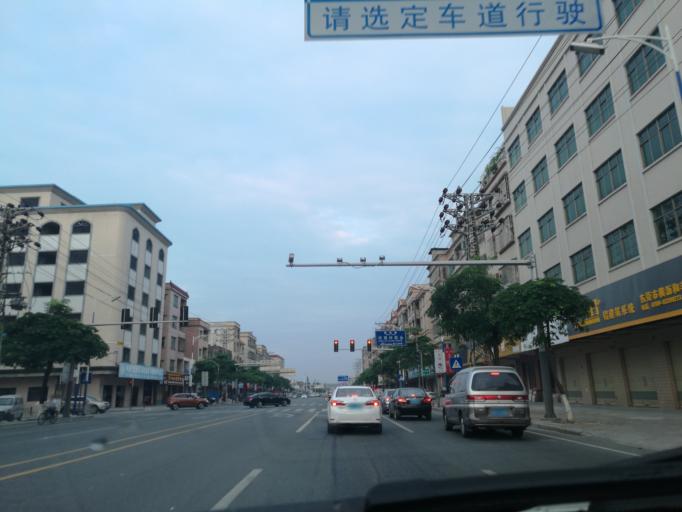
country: CN
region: Guangdong
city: Hengli
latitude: 23.0276
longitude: 113.9802
